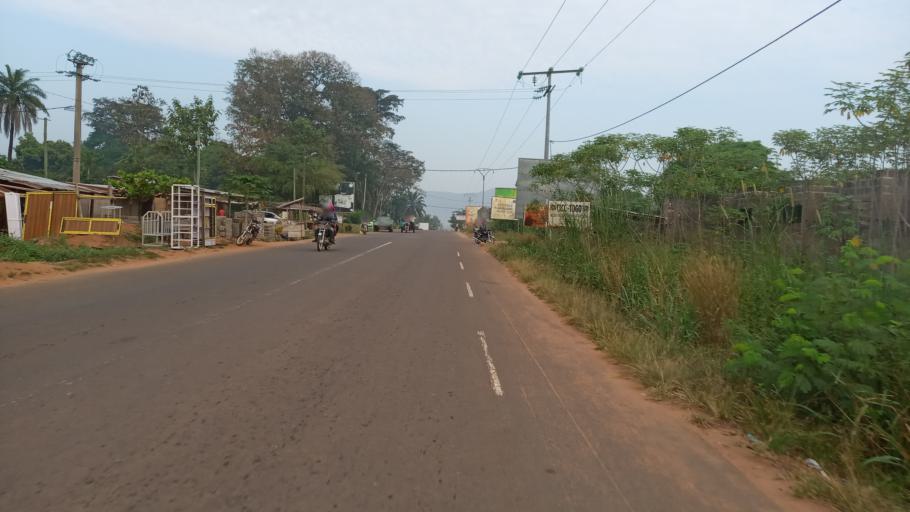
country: TG
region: Plateaux
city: Kpalime
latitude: 6.8908
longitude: 0.6415
